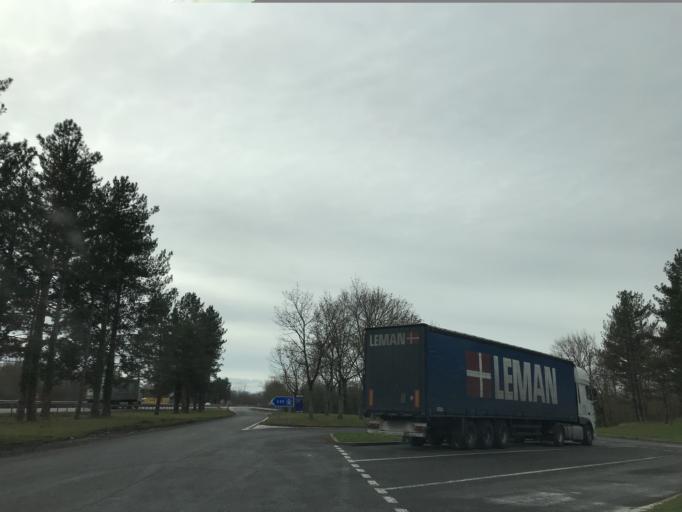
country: FR
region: Auvergne
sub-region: Departement du Puy-de-Dome
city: Culhat
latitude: 45.8351
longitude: 3.2974
